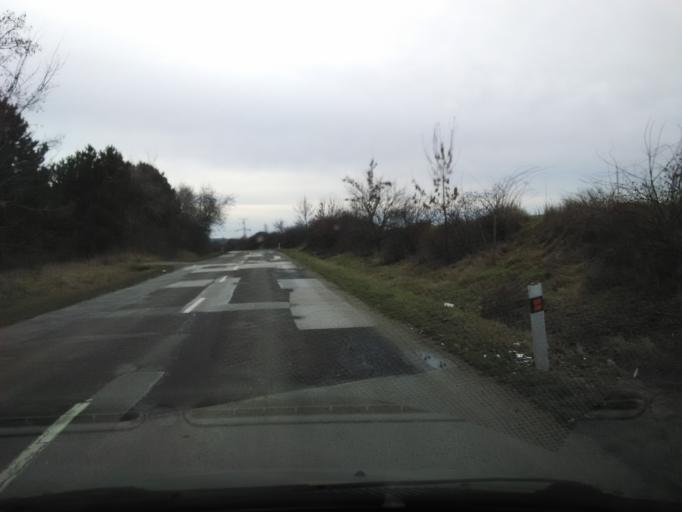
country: SK
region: Nitriansky
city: Tlmace
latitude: 48.2597
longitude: 18.4415
